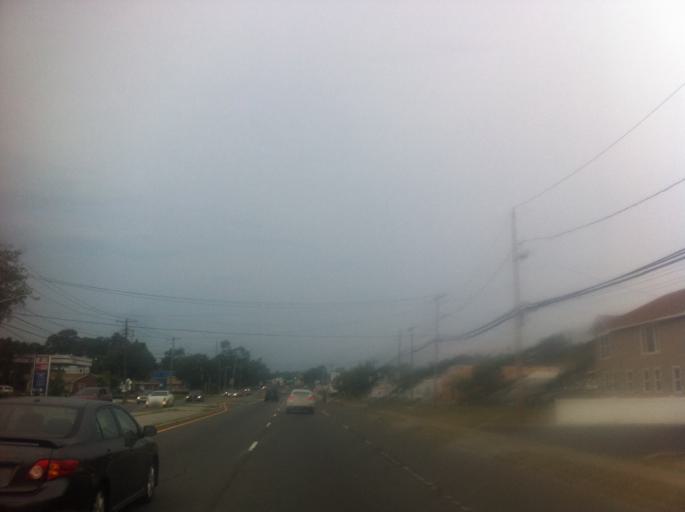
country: US
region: New York
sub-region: Suffolk County
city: North Amityville
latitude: 40.6959
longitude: -73.4243
